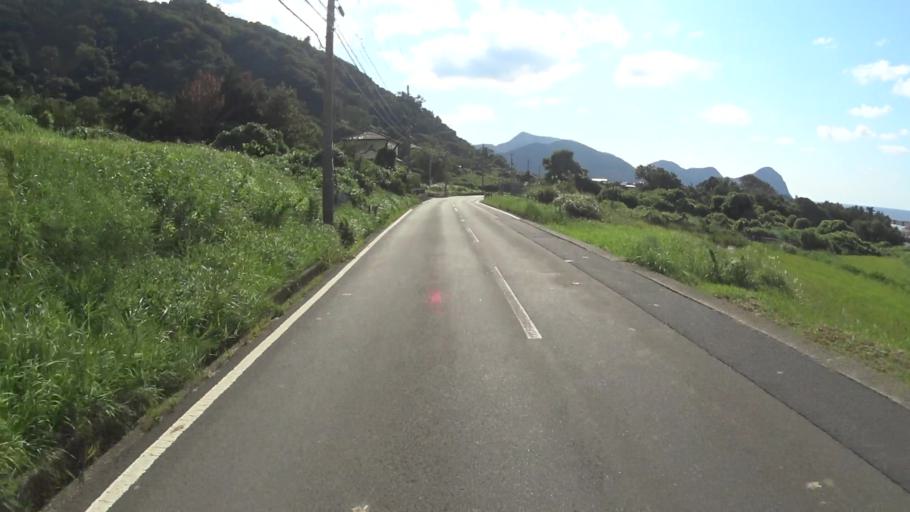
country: JP
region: Kyoto
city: Miyazu
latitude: 35.7613
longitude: 135.1872
